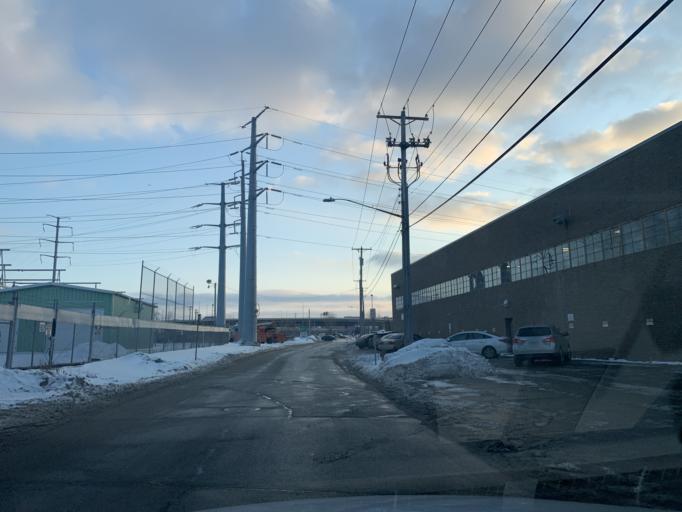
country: US
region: Minnesota
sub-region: Hennepin County
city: Minneapolis
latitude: 44.9781
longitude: -93.2916
